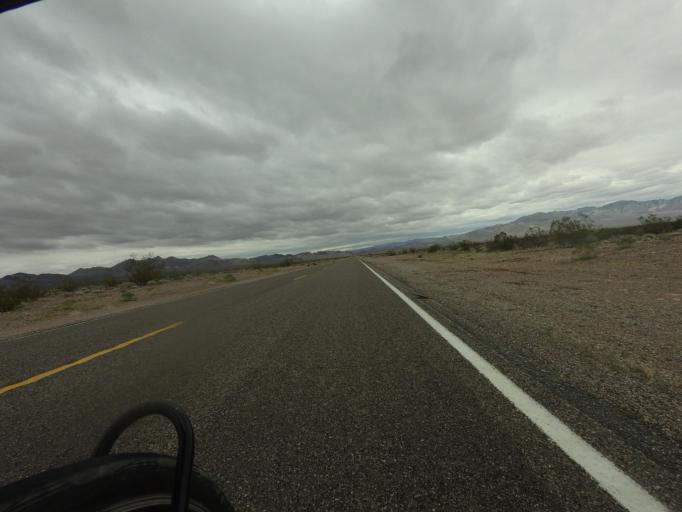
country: US
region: Nevada
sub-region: Nye County
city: Beatty
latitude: 36.8393
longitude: -116.8712
